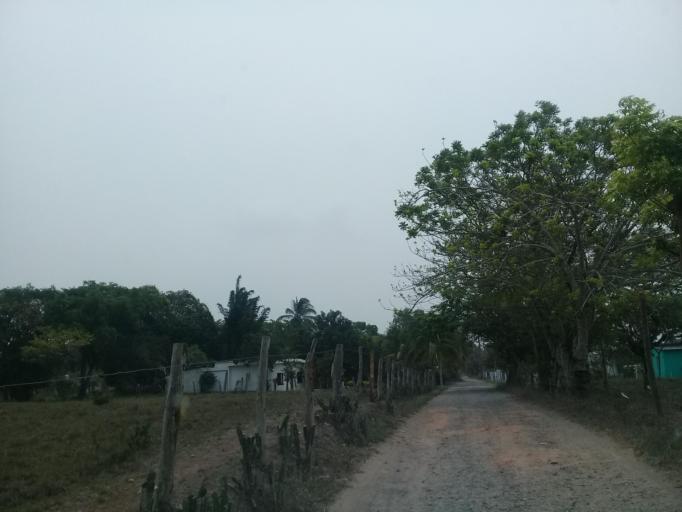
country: MX
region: Veracruz
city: Jamapa
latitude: 18.9555
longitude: -96.2042
